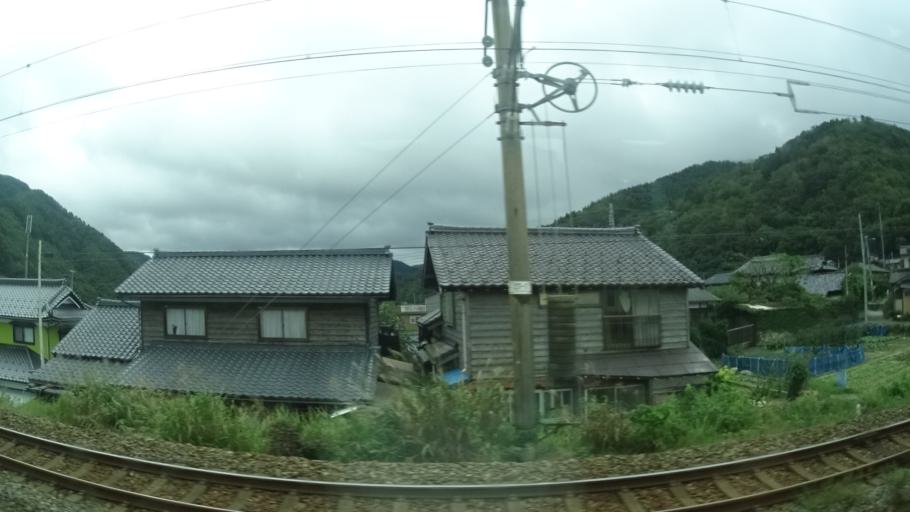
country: JP
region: Niigata
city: Murakami
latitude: 38.4520
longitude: 139.4943
